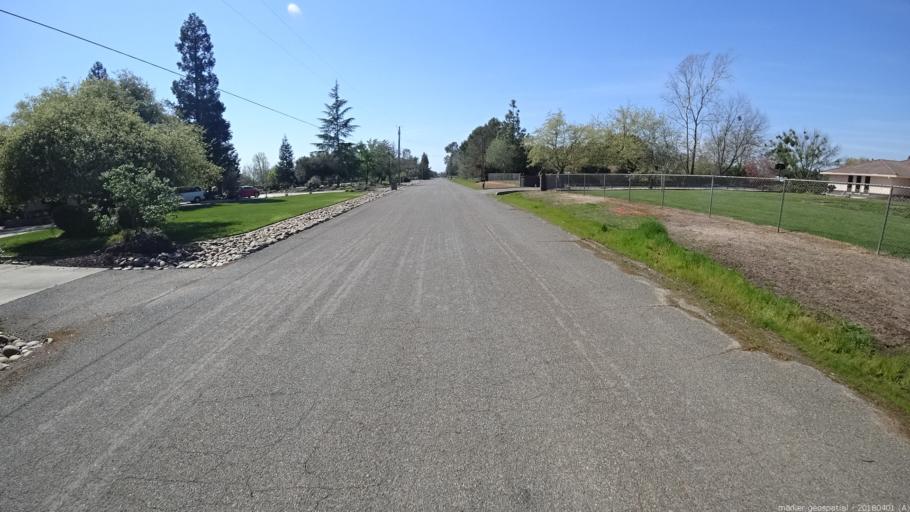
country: US
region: California
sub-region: Sacramento County
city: Wilton
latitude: 38.4032
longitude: -121.2357
